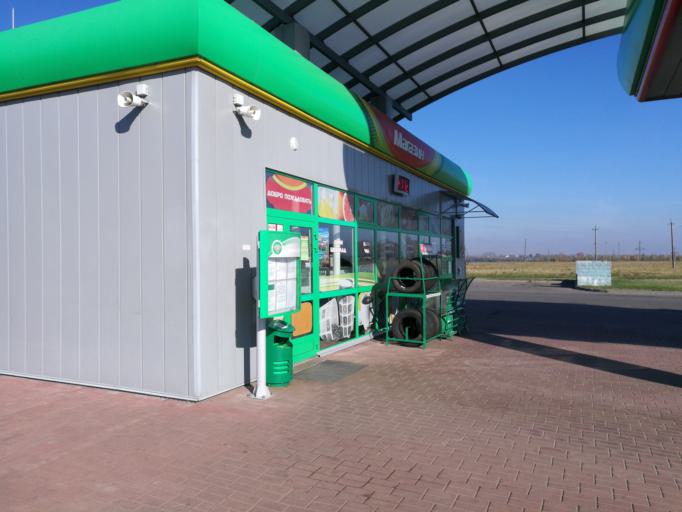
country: BY
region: Minsk
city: Krupki
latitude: 54.3208
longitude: 29.1142
